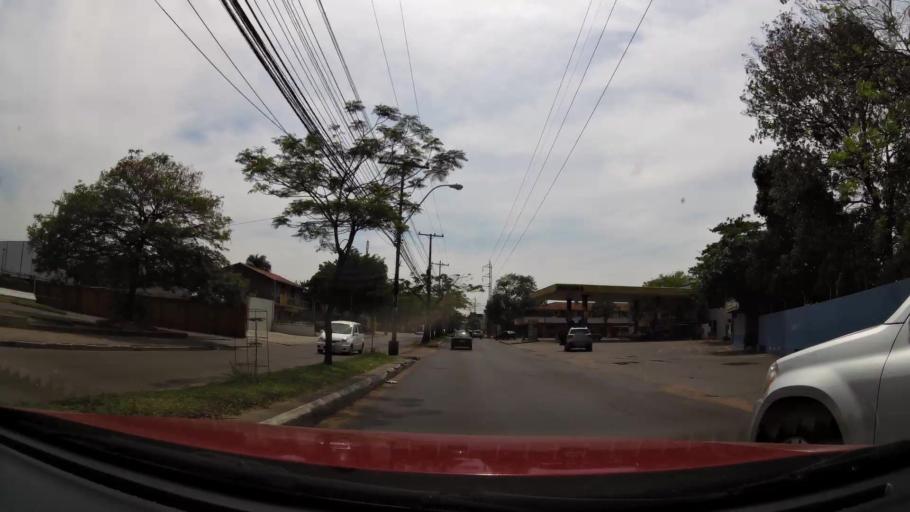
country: PY
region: Asuncion
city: Asuncion
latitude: -25.2599
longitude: -57.5888
